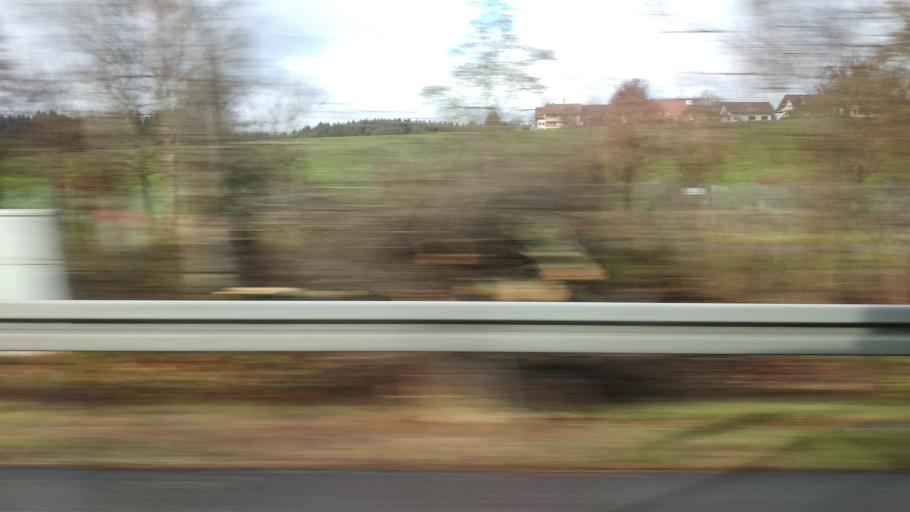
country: DE
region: Bavaria
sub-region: Swabia
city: Weissensberg
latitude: 47.6233
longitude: 9.7388
